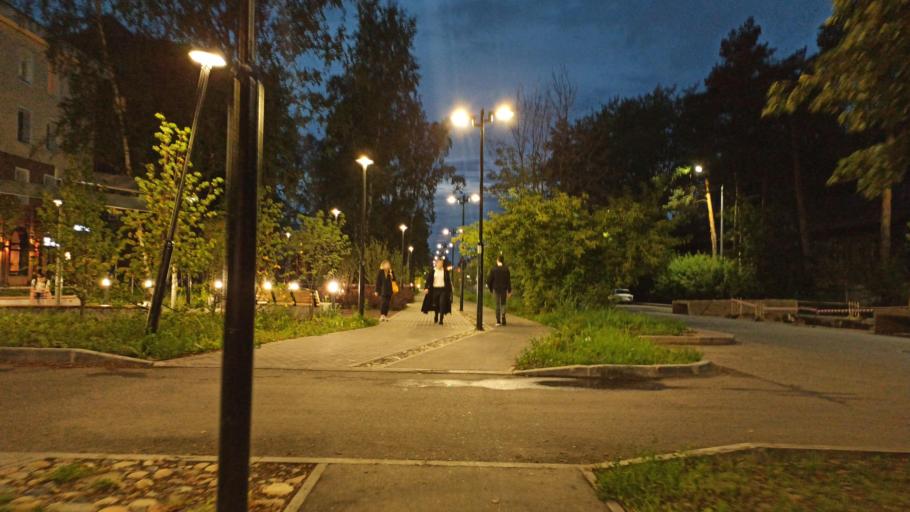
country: RU
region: Tomsk
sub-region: Tomskiy Rayon
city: Tomsk
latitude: 56.4639
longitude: 84.9625
